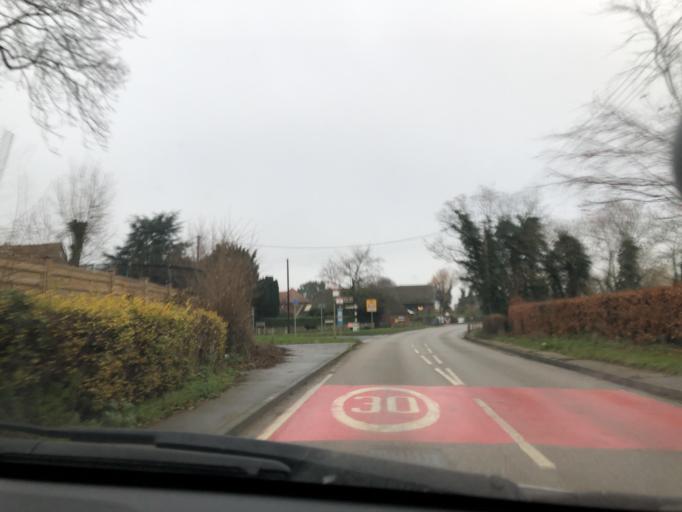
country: GB
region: England
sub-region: Kent
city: Longfield
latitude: 51.4121
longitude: 0.3295
